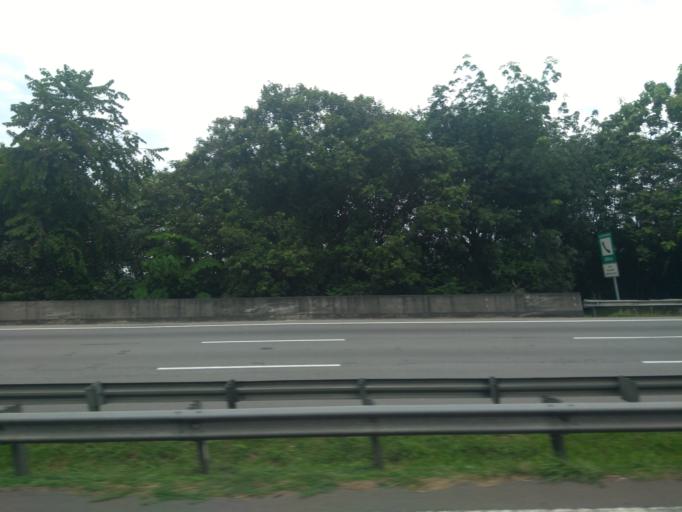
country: MY
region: Melaka
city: Pulau Sebang
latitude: 2.4449
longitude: 102.1798
